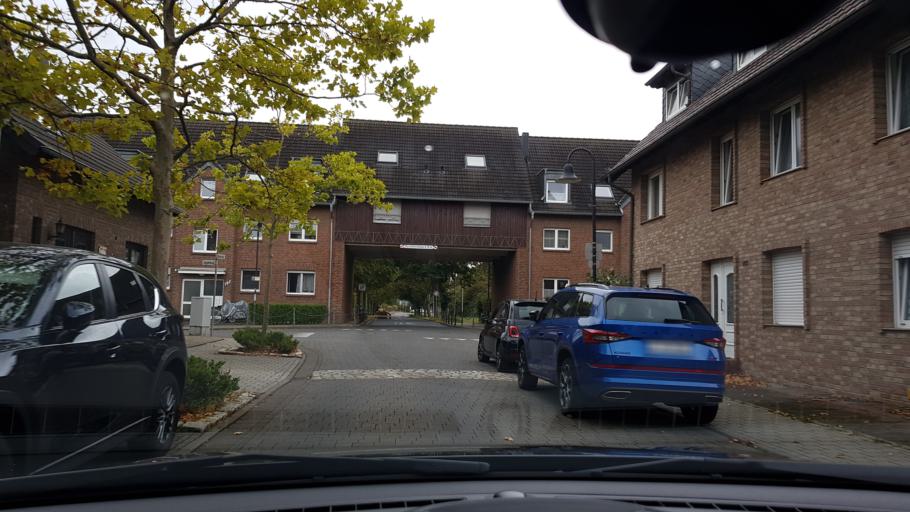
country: DE
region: North Rhine-Westphalia
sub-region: Regierungsbezirk Koln
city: Elsdorf
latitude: 50.9447
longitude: 6.5642
